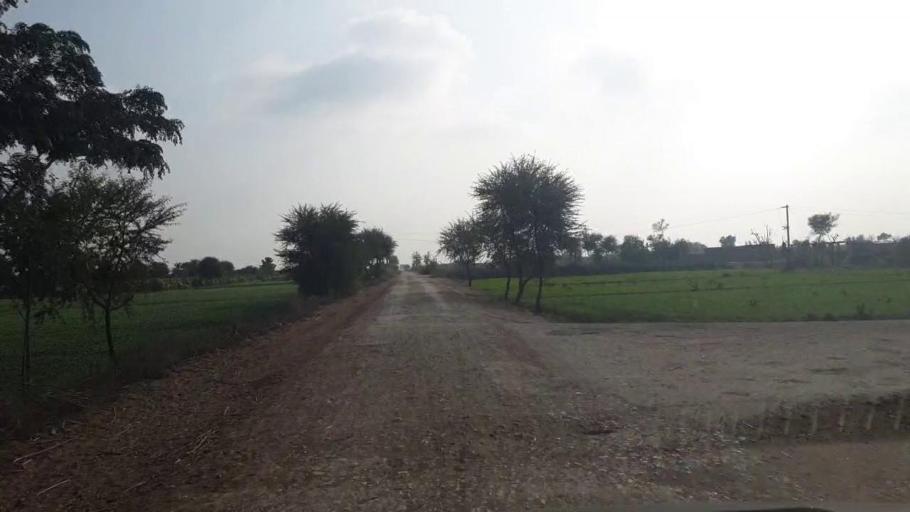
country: PK
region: Sindh
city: Shahdadpur
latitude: 25.8849
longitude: 68.6677
